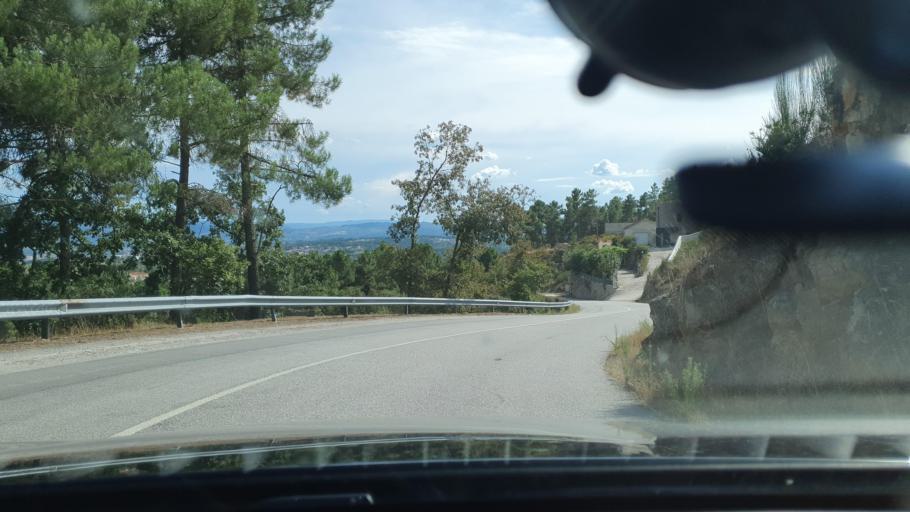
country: PT
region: Vila Real
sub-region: Chaves
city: Chaves
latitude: 41.7819
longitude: -7.4941
